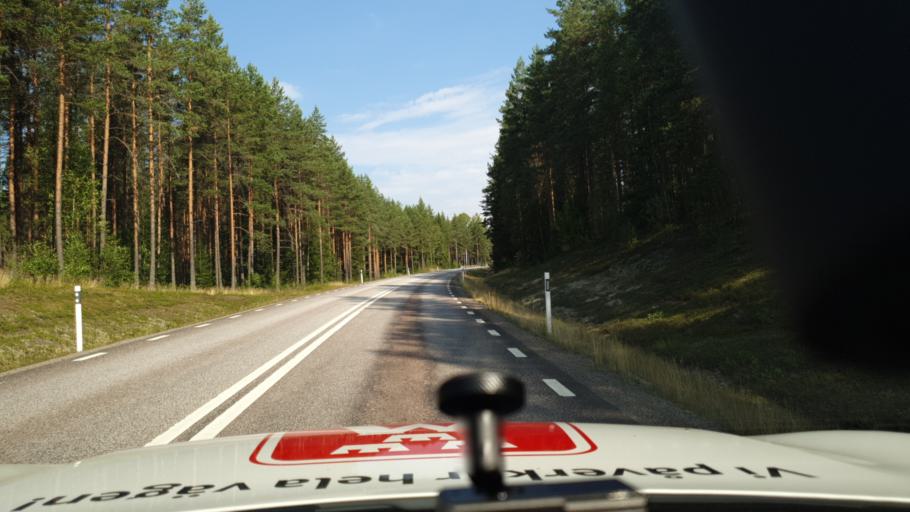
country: SE
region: Vaermland
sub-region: Hagfors Kommun
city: Ekshaerad
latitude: 60.4270
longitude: 13.2563
